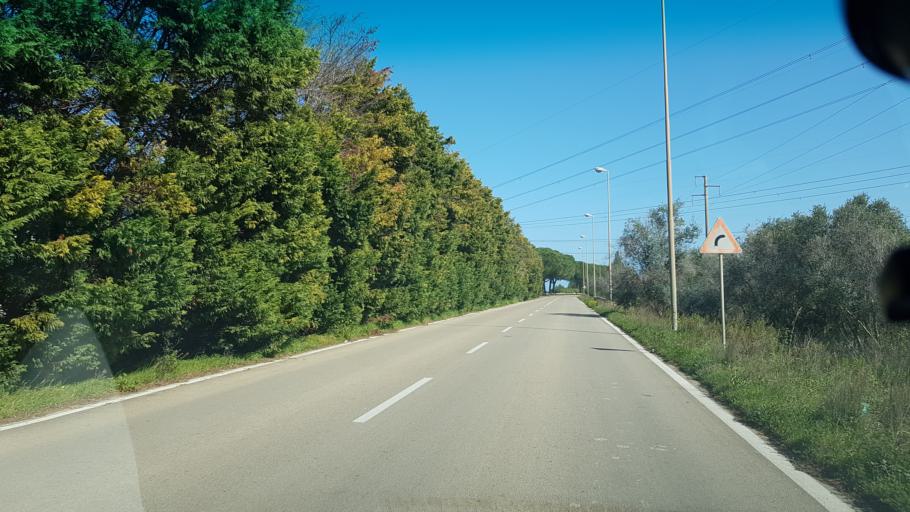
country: IT
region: Apulia
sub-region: Provincia di Brindisi
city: San Pietro Vernotico
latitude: 40.5568
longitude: 18.0311
